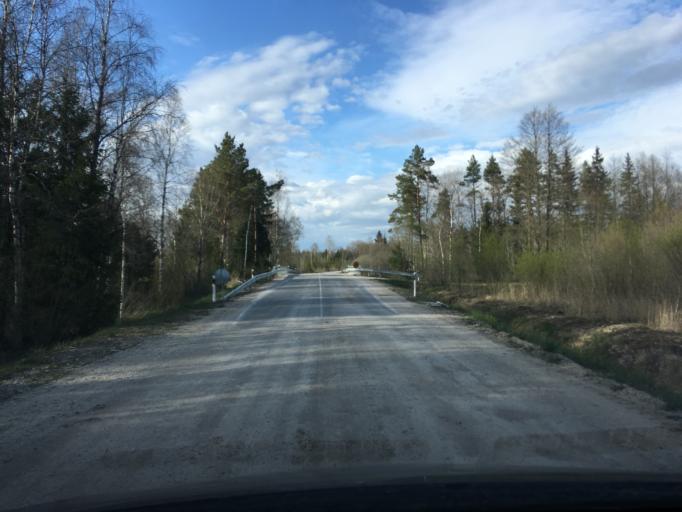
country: EE
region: Raplamaa
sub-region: Maerjamaa vald
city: Marjamaa
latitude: 58.9925
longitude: 24.3670
